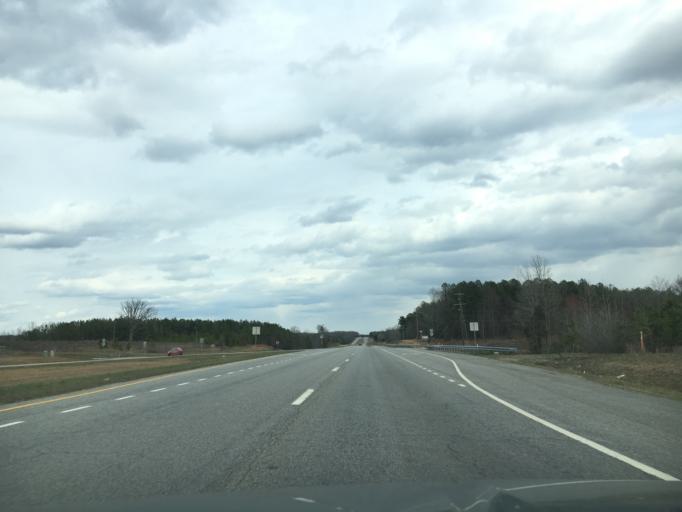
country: US
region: Virginia
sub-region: Mecklenburg County
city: Boydton
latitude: 36.6747
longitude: -78.3728
